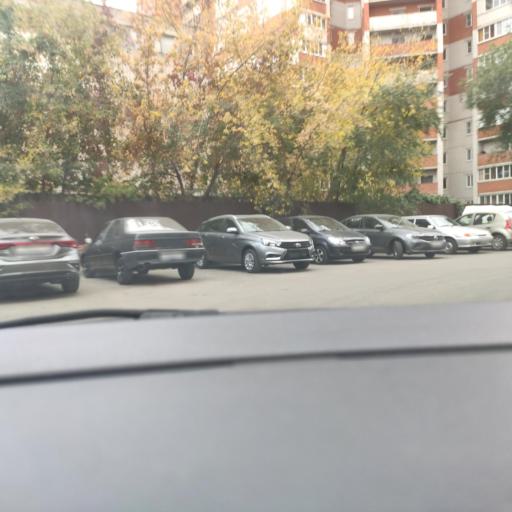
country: RU
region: Voronezj
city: Voronezh
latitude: 51.7046
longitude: 39.1925
